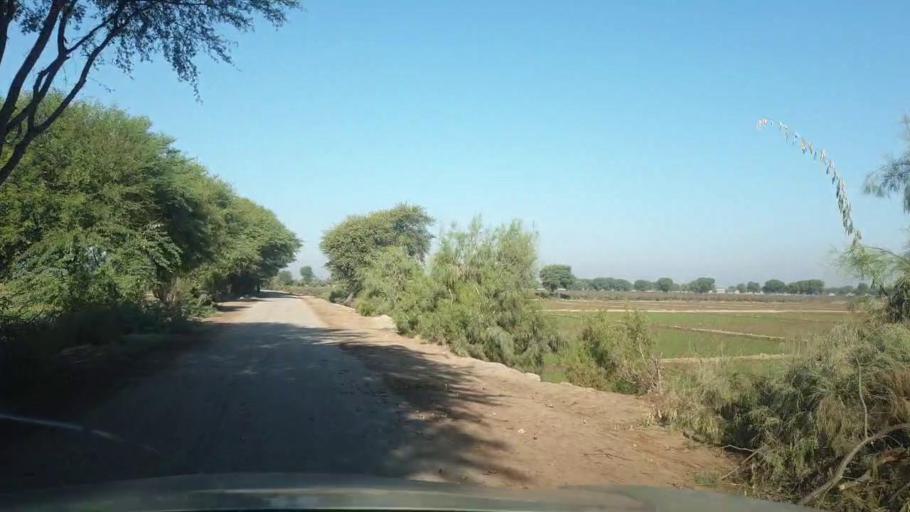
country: PK
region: Sindh
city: Bhan
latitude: 26.5492
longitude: 67.6668
